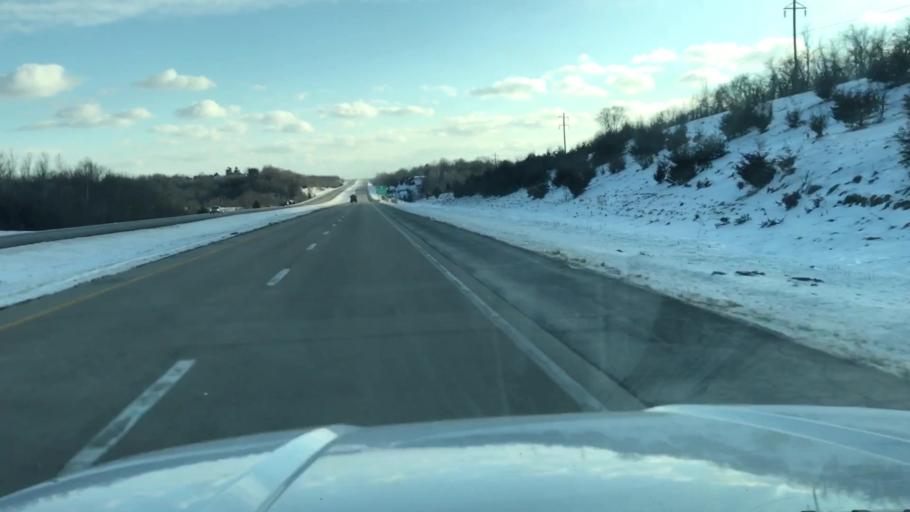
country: US
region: Missouri
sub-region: Andrew County
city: Savannah
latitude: 39.9437
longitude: -94.8603
